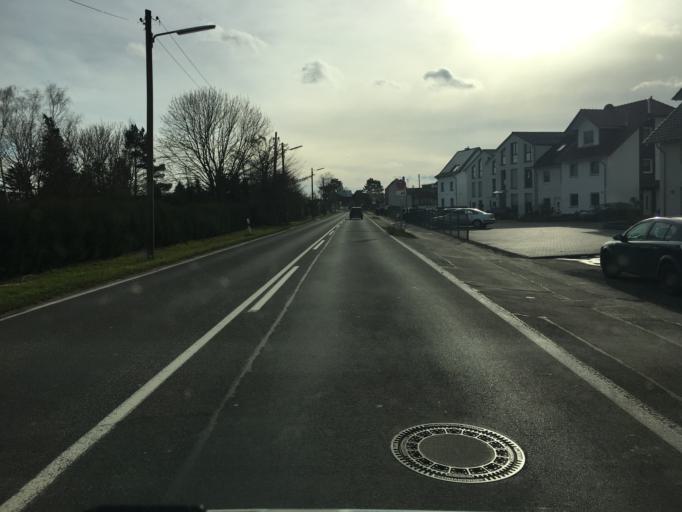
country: DE
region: North Rhine-Westphalia
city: Niederkassel
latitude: 50.7952
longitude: 7.0221
